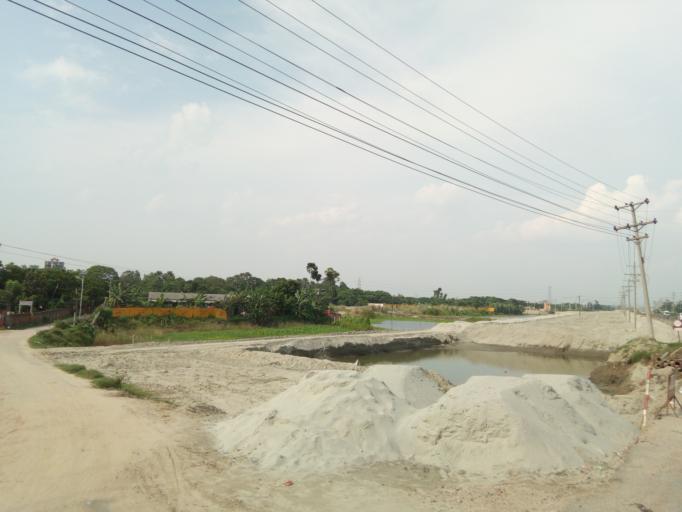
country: BD
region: Dhaka
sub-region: Dhaka
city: Dhaka
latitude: 23.6638
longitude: 90.3914
